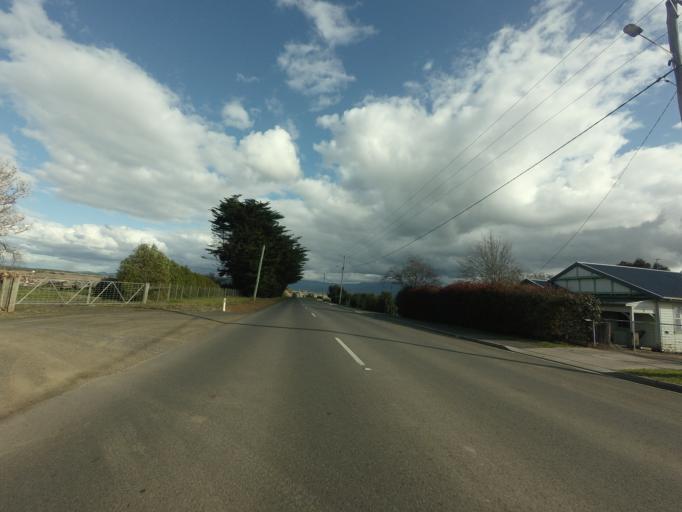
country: AU
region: Tasmania
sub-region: Northern Midlands
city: Longford
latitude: -41.6953
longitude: 147.0783
